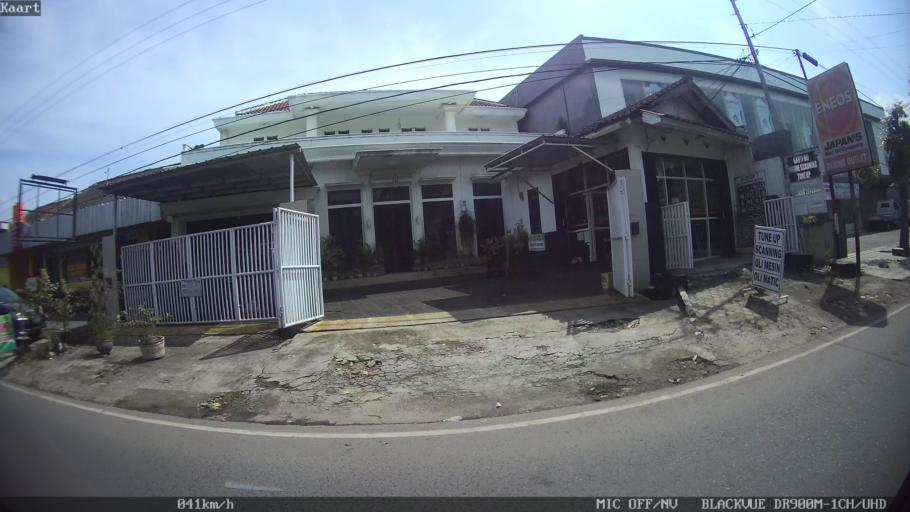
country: ID
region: Lampung
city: Kedaton
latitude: -5.3797
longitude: 105.2645
